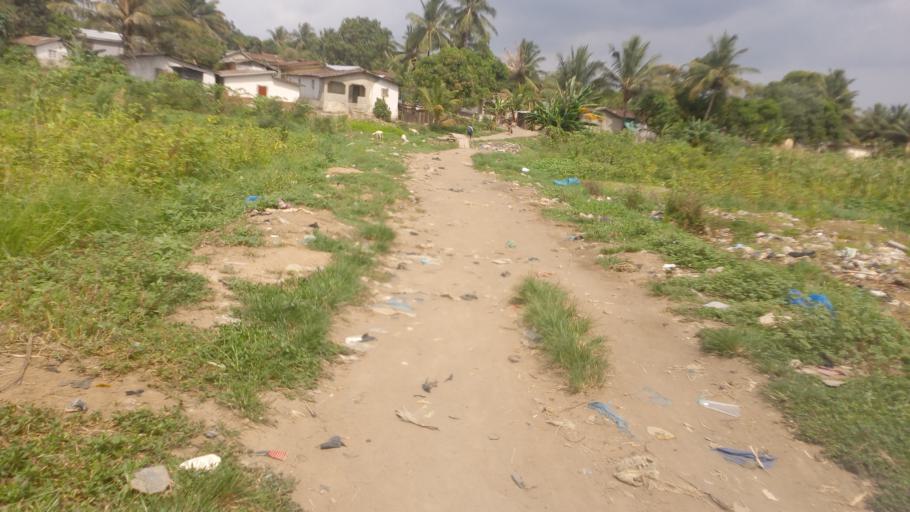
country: SL
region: Western Area
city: Waterloo
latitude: 8.3230
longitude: -13.0603
